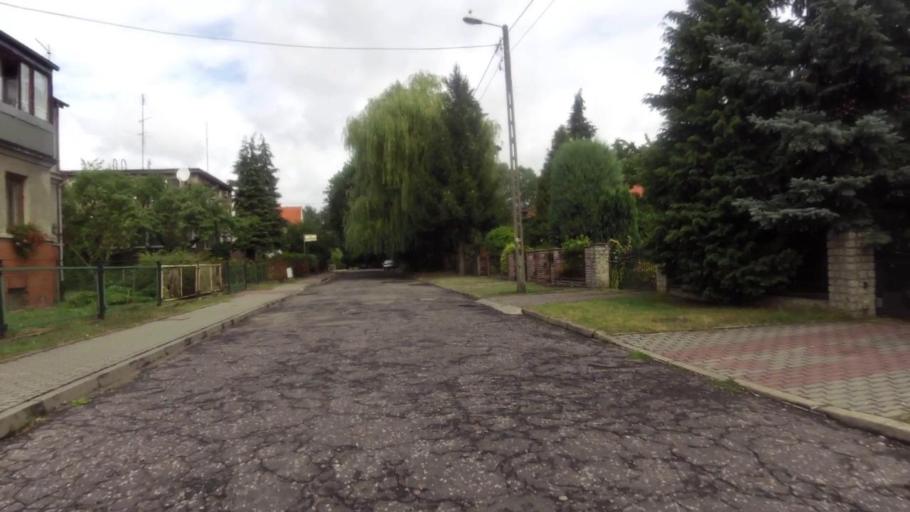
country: PL
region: West Pomeranian Voivodeship
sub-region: Powiat mysliborski
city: Debno
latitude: 52.7408
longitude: 14.7030
